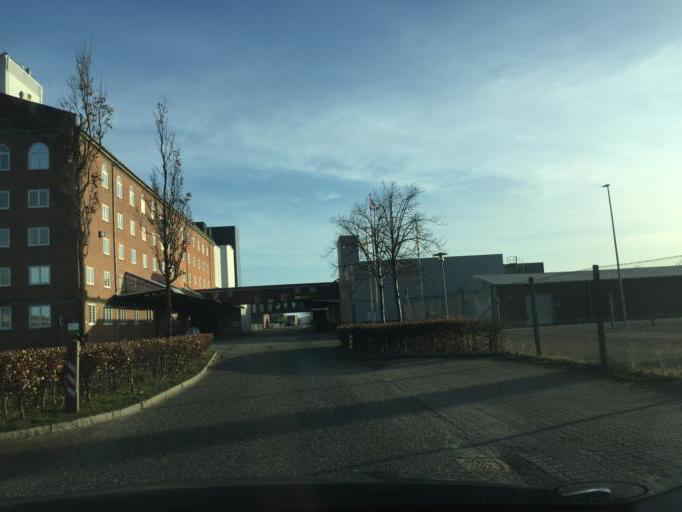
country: DK
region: South Denmark
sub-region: Vejle Kommune
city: Vejle
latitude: 55.7048
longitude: 9.5458
